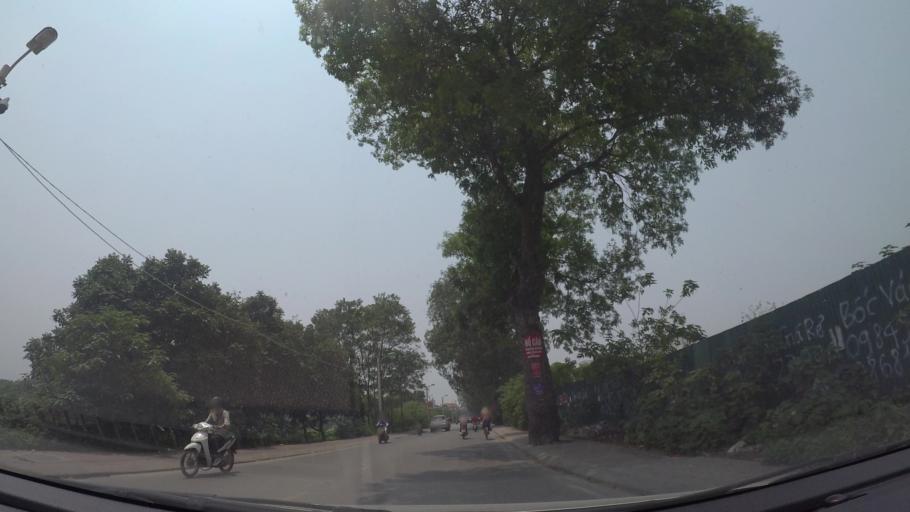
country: VN
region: Ha Noi
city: Thanh Xuan
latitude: 20.9909
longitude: 105.7825
